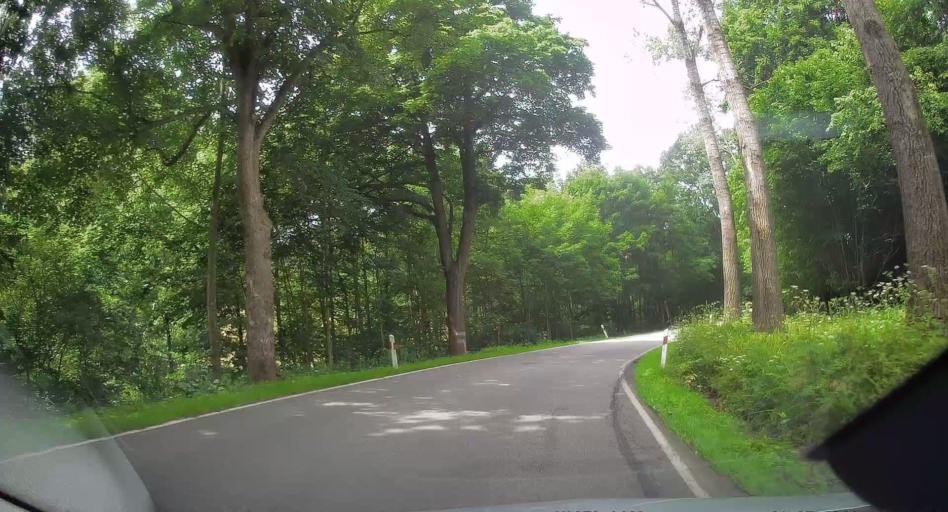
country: PL
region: Lower Silesian Voivodeship
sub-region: Powiat walbrzyski
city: Jedlina-Zdroj
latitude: 50.7323
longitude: 16.3620
